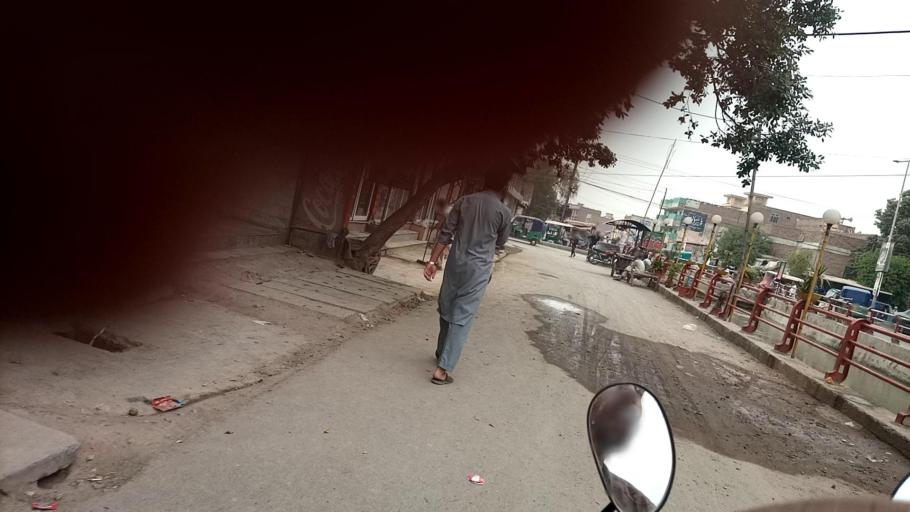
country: PK
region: Khyber Pakhtunkhwa
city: Peshawar
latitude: 34.0221
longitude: 71.5917
